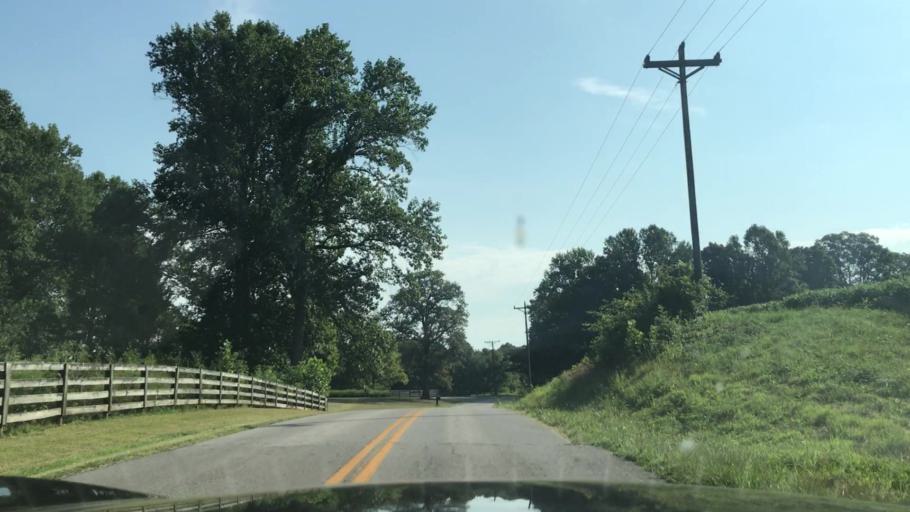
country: US
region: Kentucky
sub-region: Hart County
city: Horse Cave
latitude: 37.1913
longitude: -85.7600
